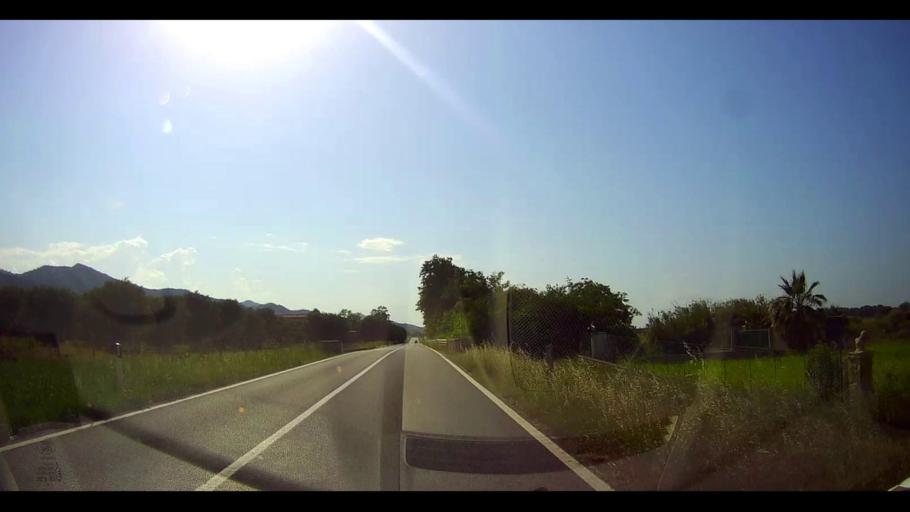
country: IT
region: Calabria
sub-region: Provincia di Cosenza
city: Cariati
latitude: 39.4795
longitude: 16.9929
